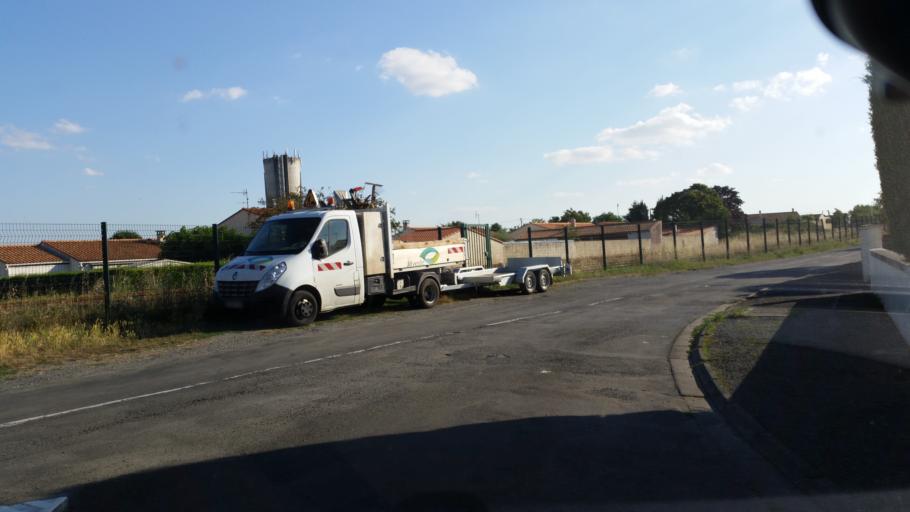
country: FR
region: Poitou-Charentes
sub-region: Departement de la Charente-Maritime
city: Marans
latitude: 46.3043
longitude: -0.9834
